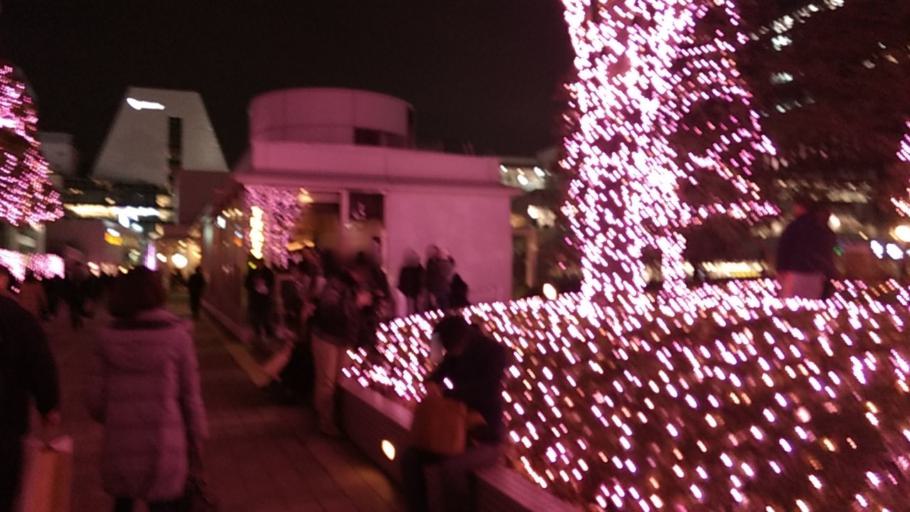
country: JP
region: Tokyo
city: Tokyo
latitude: 35.6873
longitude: 139.7004
